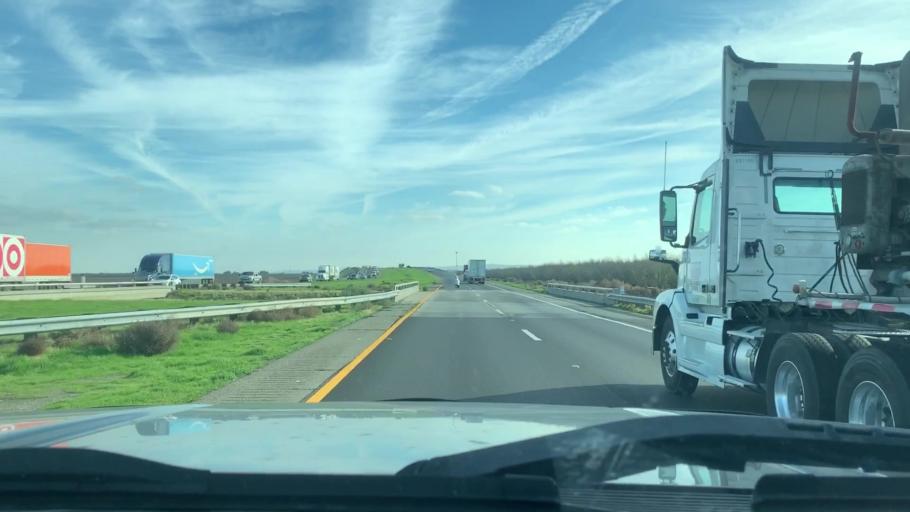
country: US
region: California
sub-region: Fresno County
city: Huron
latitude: 36.1817
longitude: -120.1984
